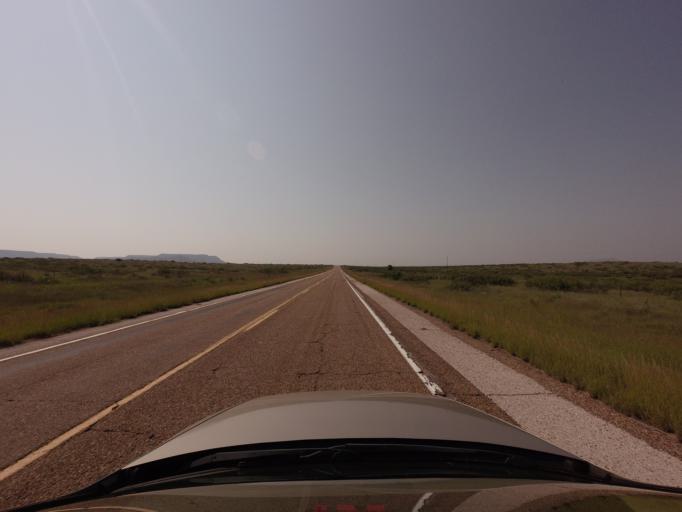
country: US
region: New Mexico
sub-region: Quay County
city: Tucumcari
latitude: 35.0309
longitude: -103.7376
